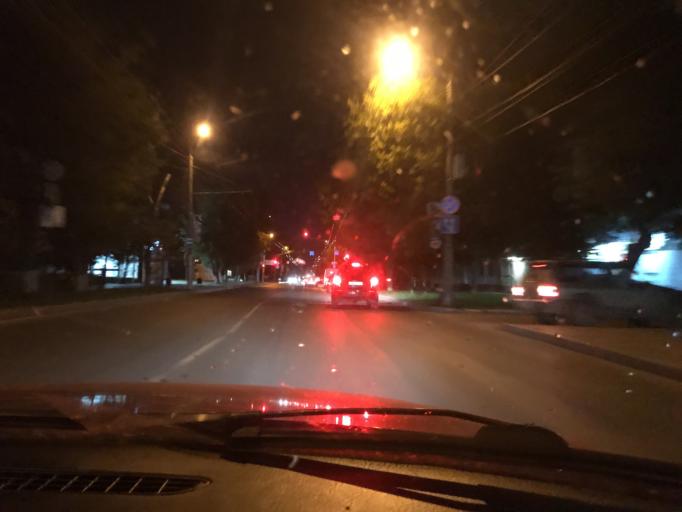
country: RU
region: Kaluga
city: Kaluga
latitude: 54.5242
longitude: 36.2660
